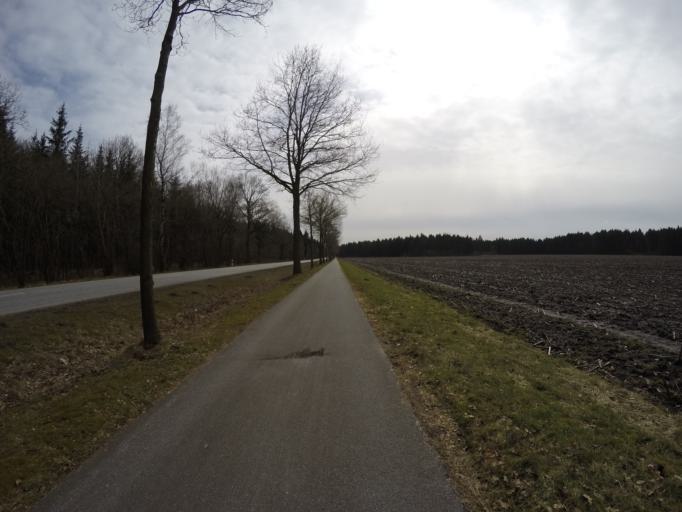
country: DE
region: Schleswig-Holstein
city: Heidmoor
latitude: 53.8262
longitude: 9.8827
